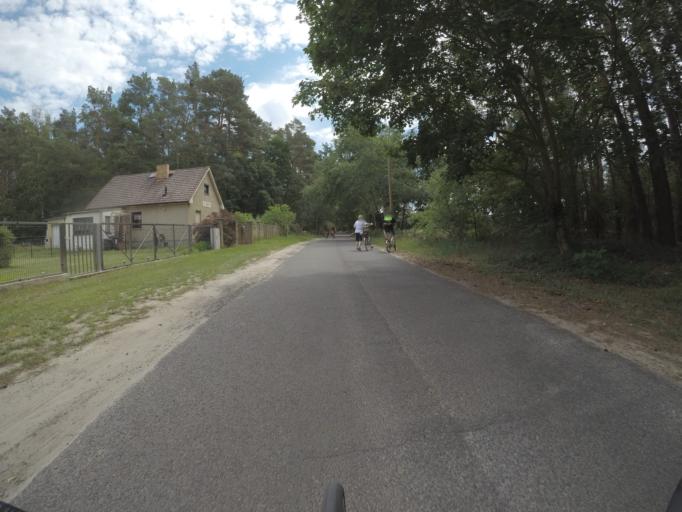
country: DE
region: Brandenburg
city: Storkow
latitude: 52.2440
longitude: 13.9571
